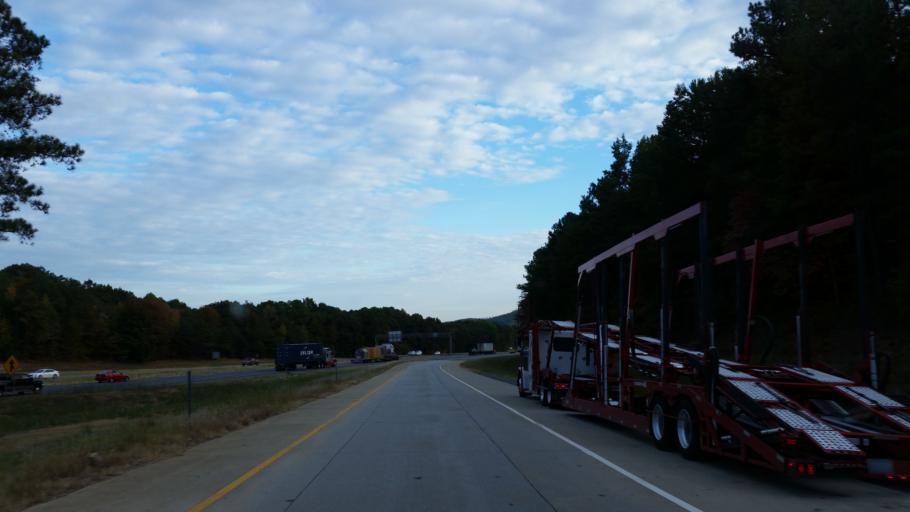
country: US
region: Georgia
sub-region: Bartow County
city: Cartersville
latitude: 34.1730
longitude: -84.7597
